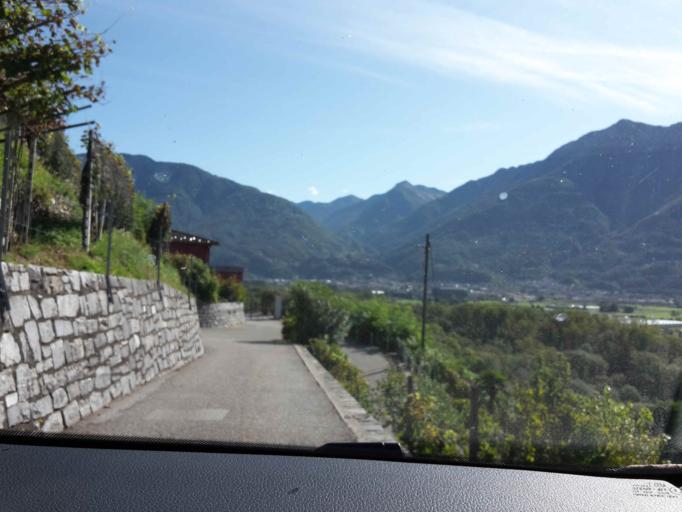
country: CH
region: Ticino
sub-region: Bellinzona District
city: Sementina
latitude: 46.1780
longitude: 8.9678
